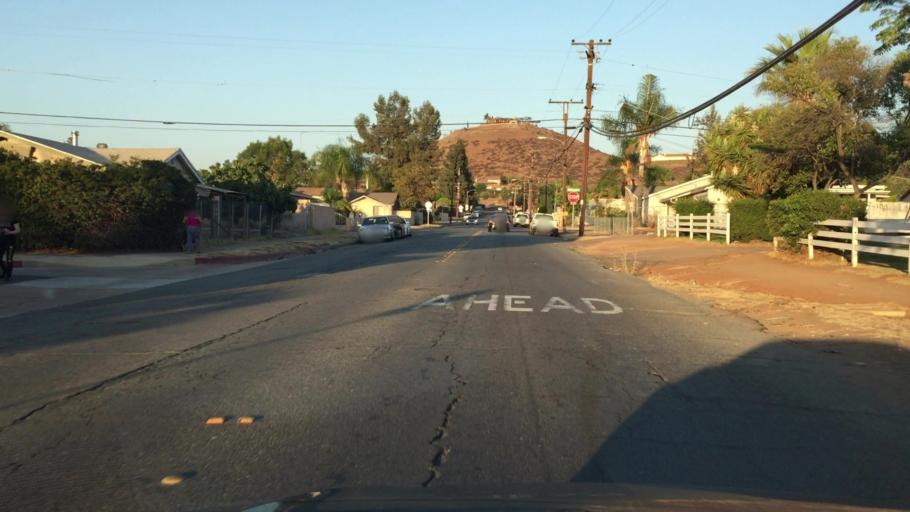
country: US
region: California
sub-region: San Diego County
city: Bostonia
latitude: 32.8191
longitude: -116.9507
